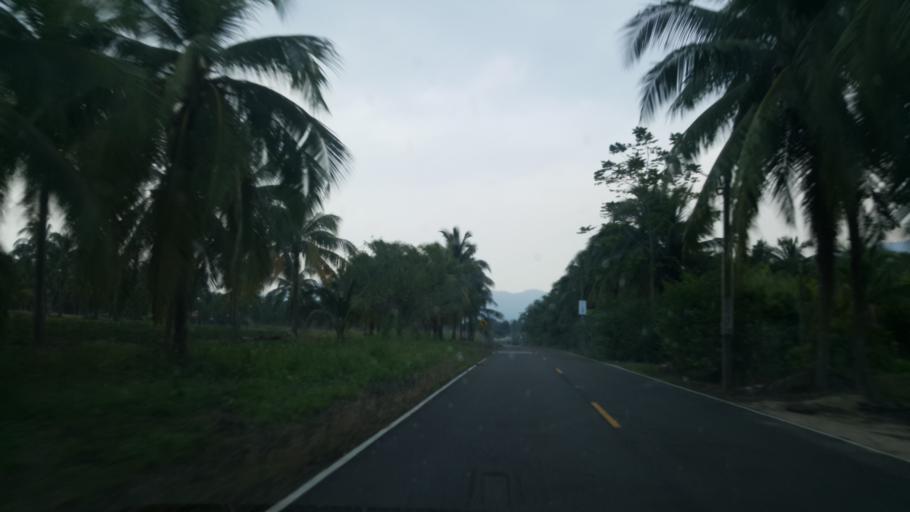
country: TH
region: Chon Buri
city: Ban Bueng
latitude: 13.2295
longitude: 101.0351
